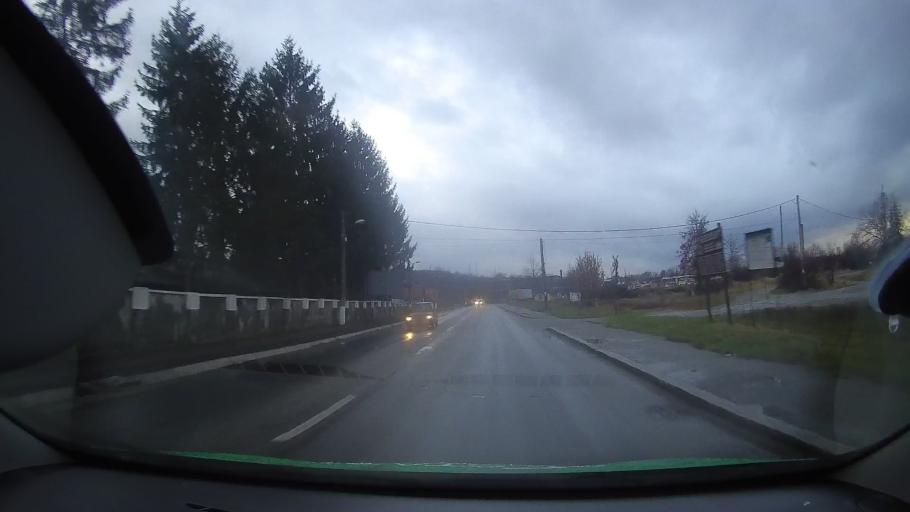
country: RO
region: Hunedoara
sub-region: Municipiul Brad
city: Brad
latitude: 46.1367
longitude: 22.7801
